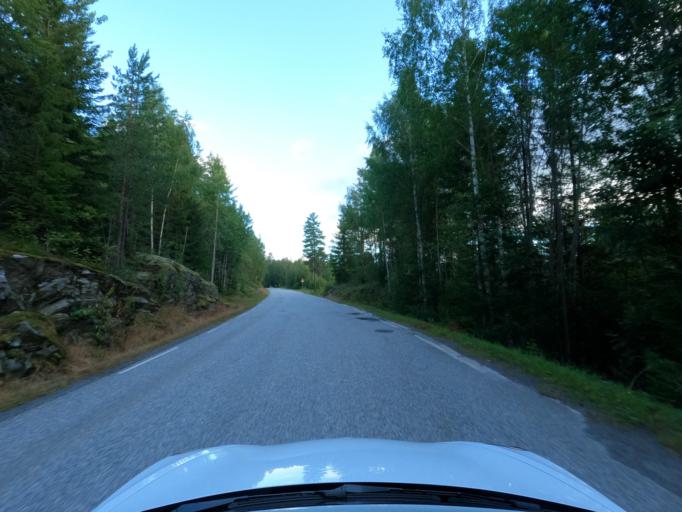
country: NO
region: Telemark
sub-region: Hjartdal
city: Sauland
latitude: 59.8100
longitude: 9.0850
